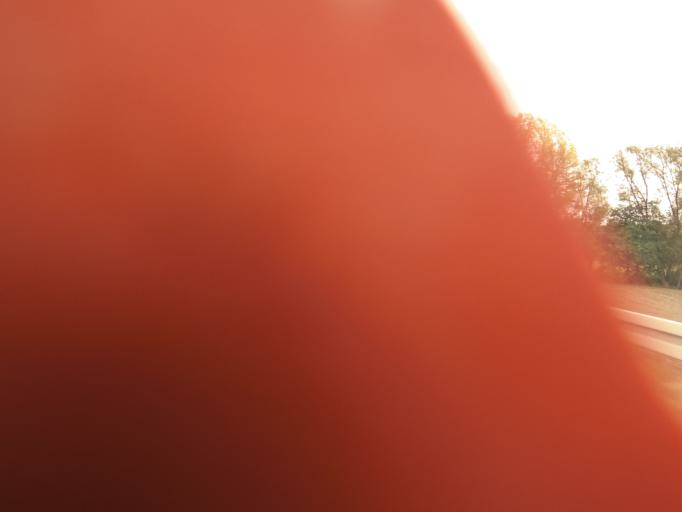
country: DE
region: Saxony-Anhalt
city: Kretzschau
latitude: 51.0562
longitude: 12.0890
